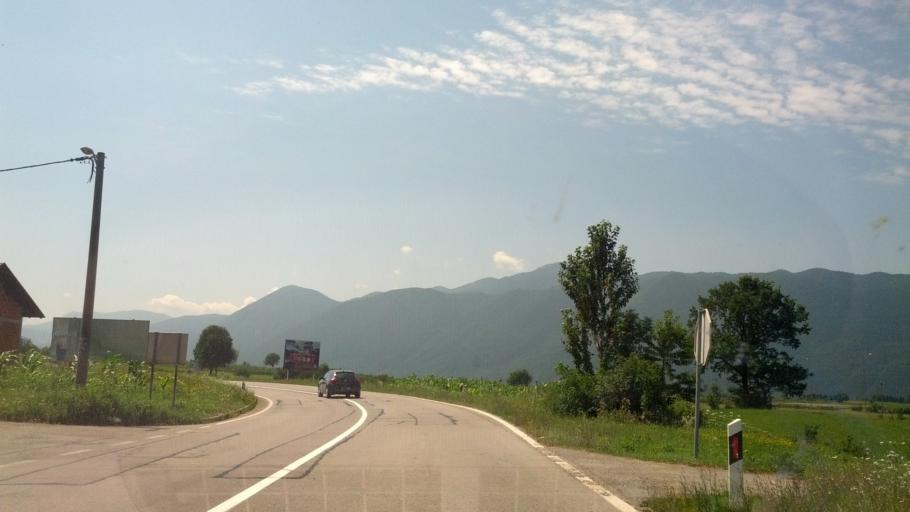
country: BA
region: Federation of Bosnia and Herzegovina
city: Izacic
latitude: 44.8743
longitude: 15.7694
